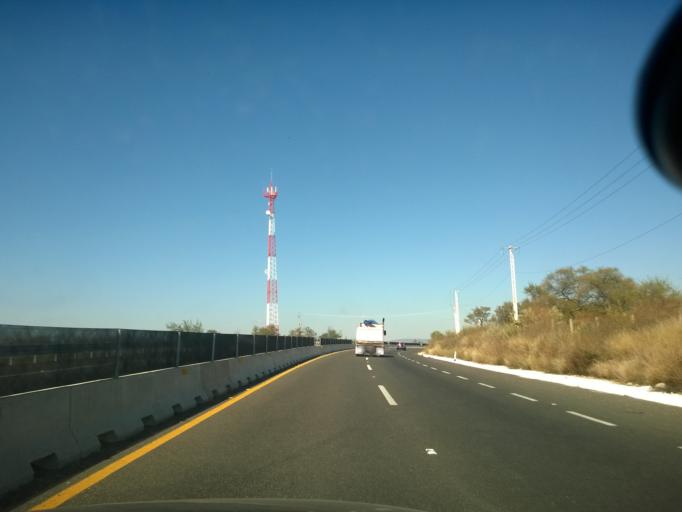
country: MX
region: Jalisco
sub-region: Lagos de Moreno
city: Geovillas Laureles del Campanario
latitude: 21.3034
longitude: -101.8752
